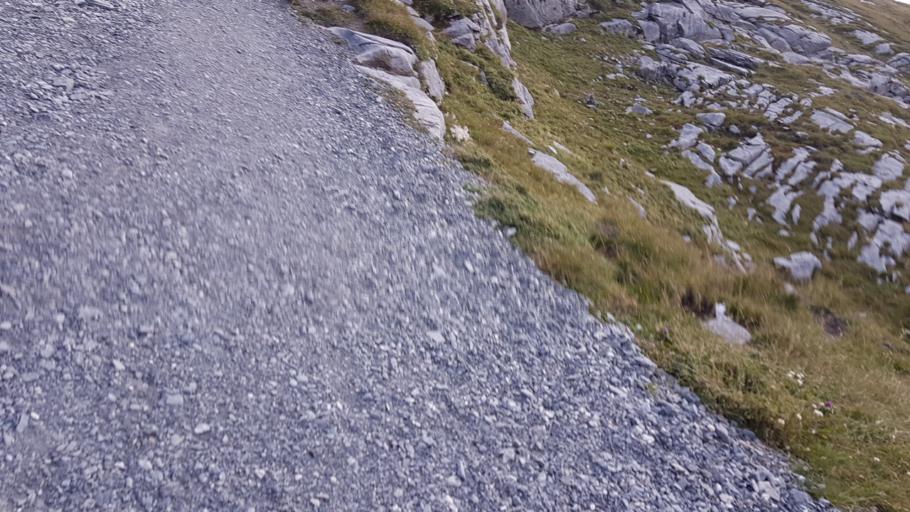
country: CH
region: Valais
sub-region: Leuk District
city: Leukerbad
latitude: 46.3985
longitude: 7.6145
